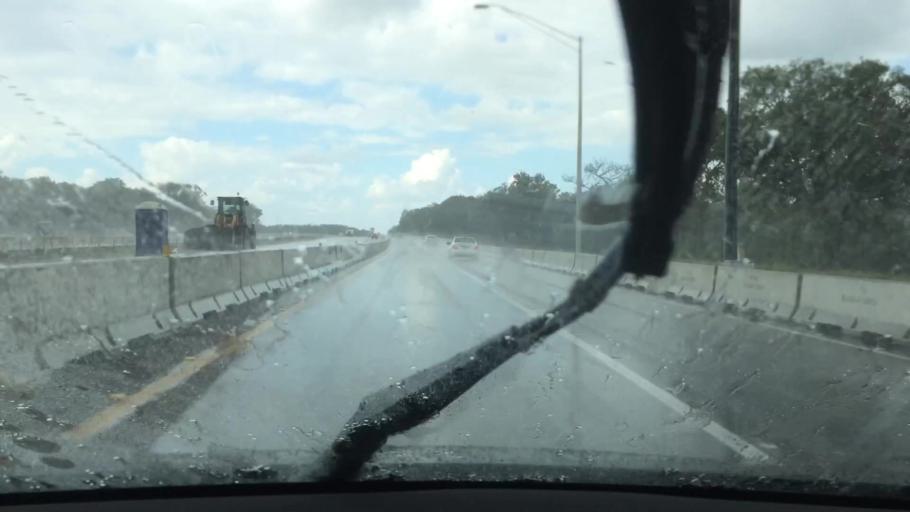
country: US
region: Florida
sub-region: Orange County
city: Wedgefield
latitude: 28.4518
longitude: -81.1034
